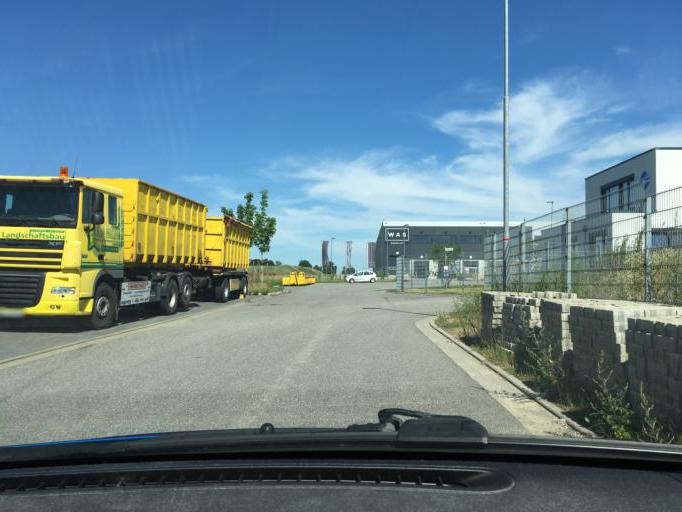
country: DE
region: Lower Saxony
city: Buchholz in der Nordheide
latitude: 53.3748
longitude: 9.9060
